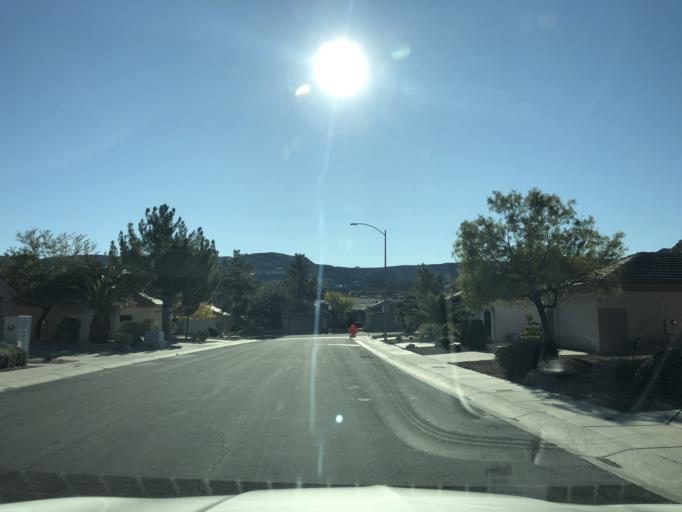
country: US
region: Nevada
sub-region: Clark County
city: Whitney
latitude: 36.0081
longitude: -115.0694
